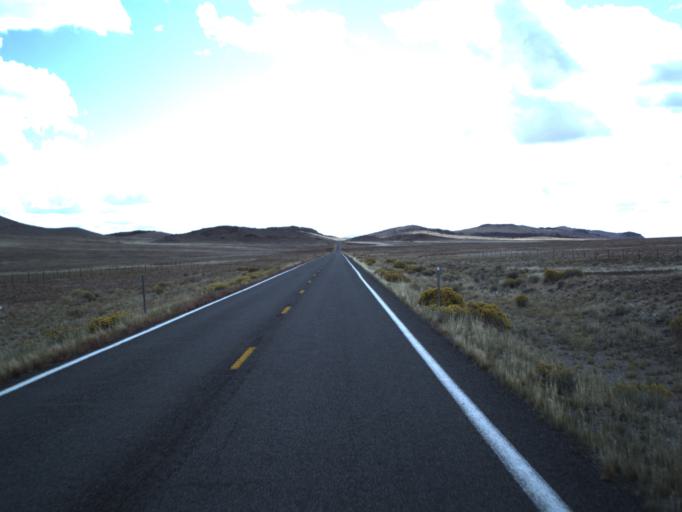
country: US
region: Utah
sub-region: Beaver County
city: Milford
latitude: 38.6456
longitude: -113.8654
